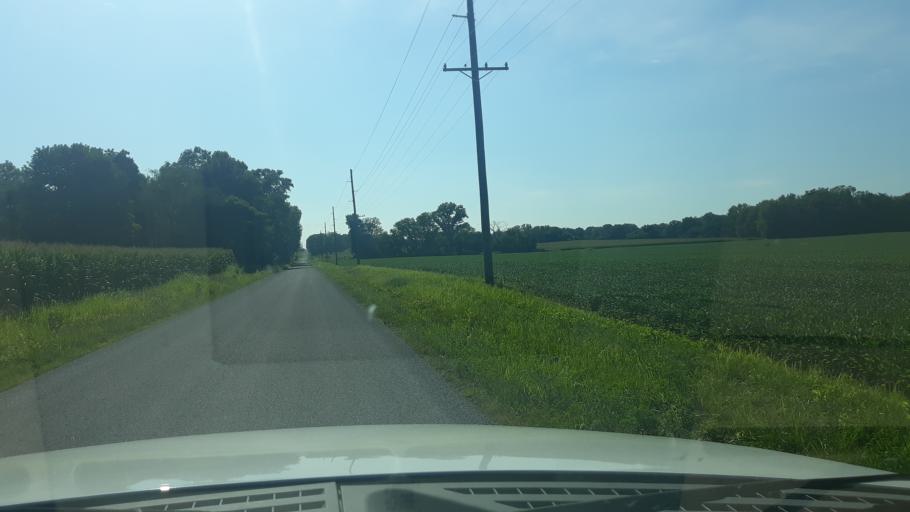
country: US
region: Illinois
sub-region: Saline County
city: Eldorado
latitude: 37.8630
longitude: -88.5222
